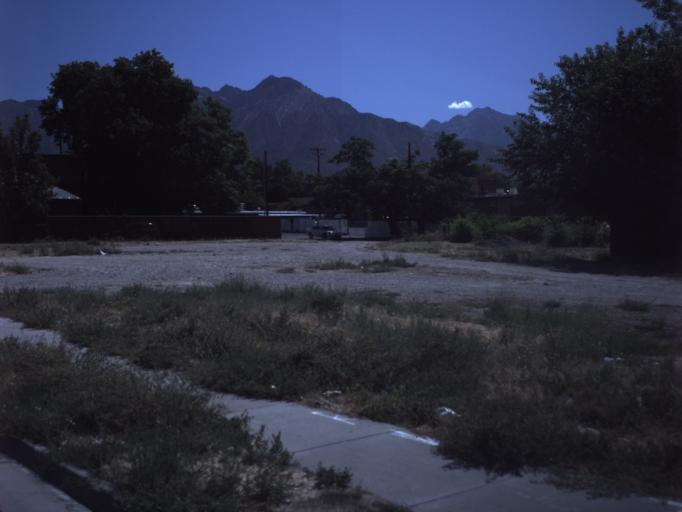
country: US
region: Utah
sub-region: Salt Lake County
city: Willard
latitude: 40.6999
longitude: -111.8537
